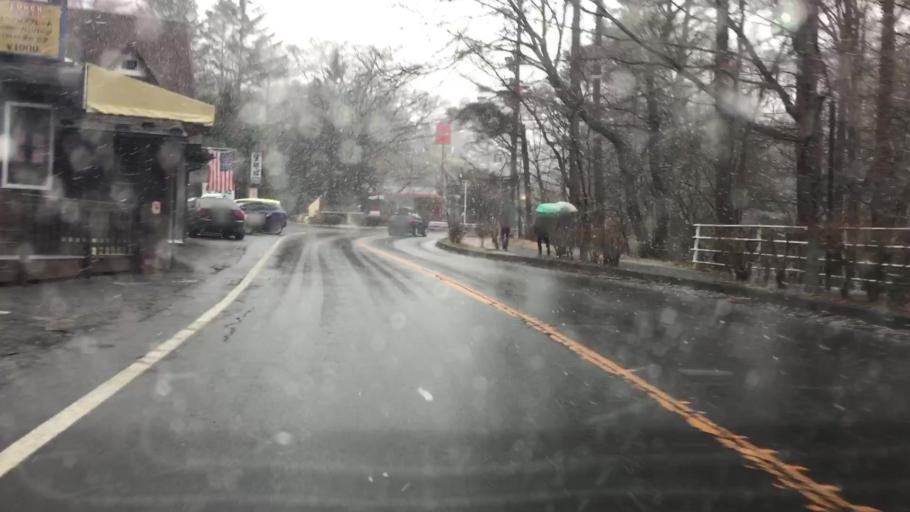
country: JP
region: Nagano
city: Komoro
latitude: 36.3602
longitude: 138.5894
